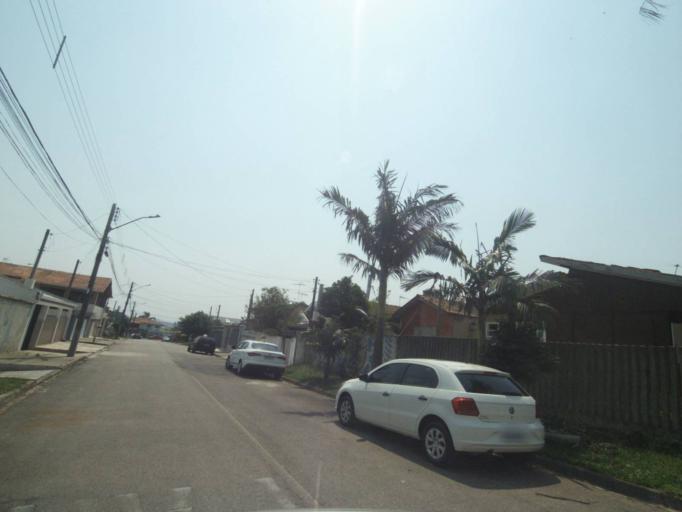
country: BR
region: Parana
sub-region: Sao Jose Dos Pinhais
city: Sao Jose dos Pinhais
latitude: -25.5420
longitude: -49.2441
